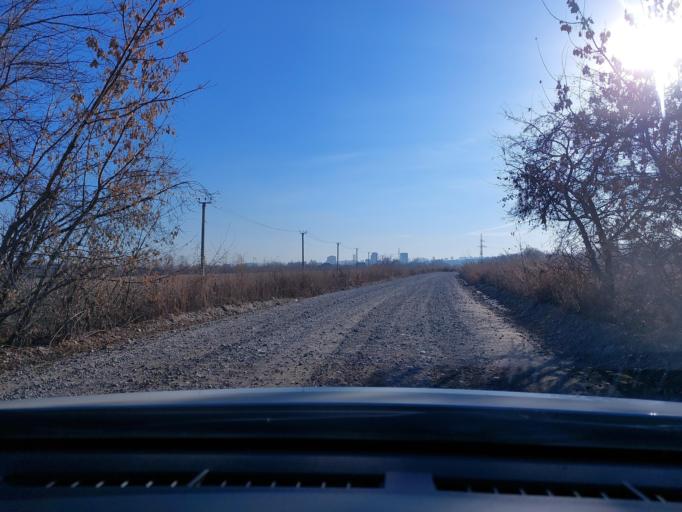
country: RU
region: Irkutsk
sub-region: Irkutskiy Rayon
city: Irkutsk
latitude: 52.3051
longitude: 104.2756
